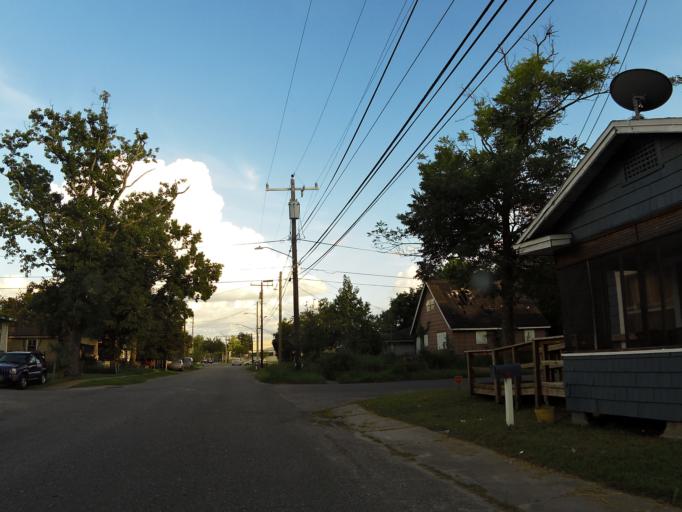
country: US
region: Florida
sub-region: Duval County
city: Jacksonville
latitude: 30.3352
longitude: -81.6912
